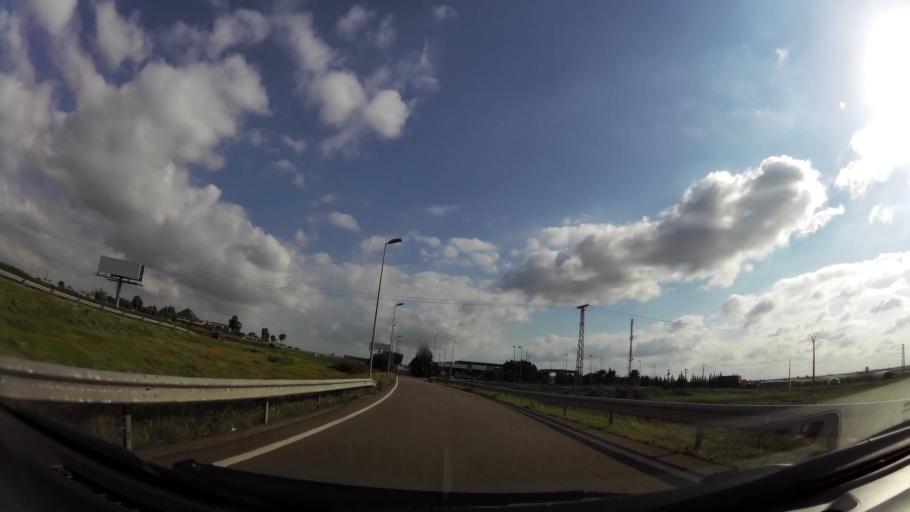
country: MA
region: Chaouia-Ouardigha
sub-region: Settat Province
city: Berrechid
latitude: 33.2247
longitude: -7.5747
